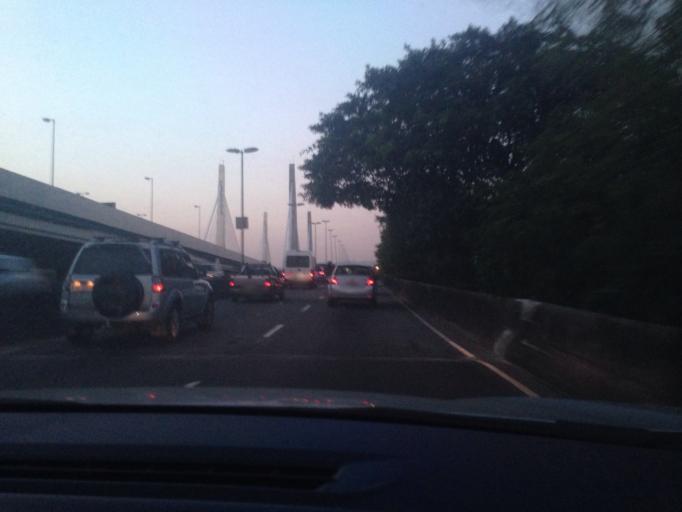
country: BR
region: Rio de Janeiro
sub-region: Sao Joao De Meriti
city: Sao Joao de Meriti
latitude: -22.9786
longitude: -43.3654
